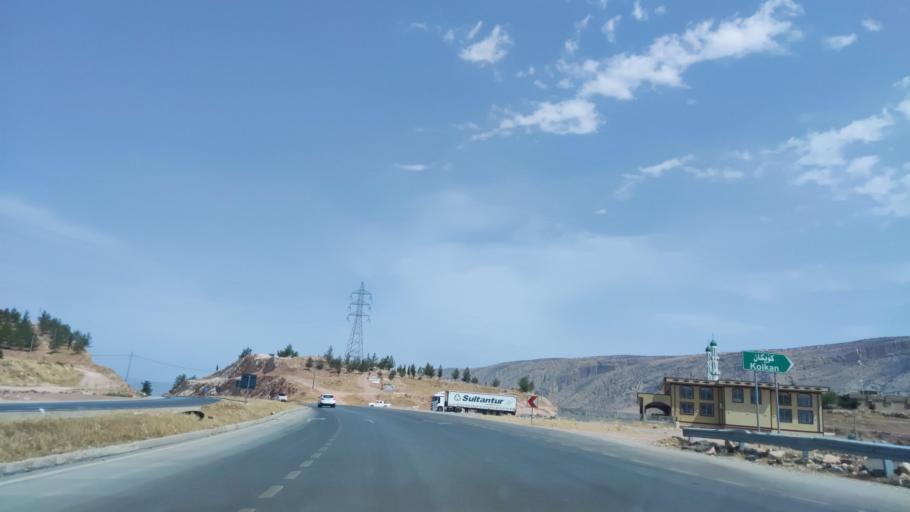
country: IQ
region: Arbil
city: Shaqlawah
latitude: 36.4859
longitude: 44.3814
